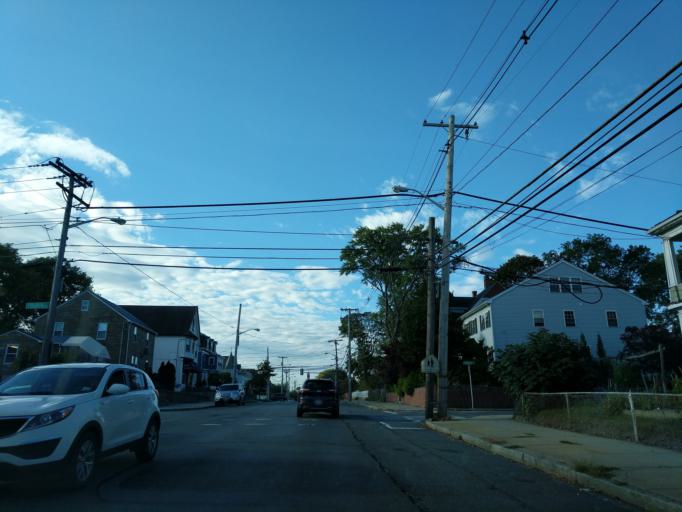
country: US
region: Massachusetts
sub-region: Middlesex County
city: Malden
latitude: 42.4099
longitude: -71.0798
